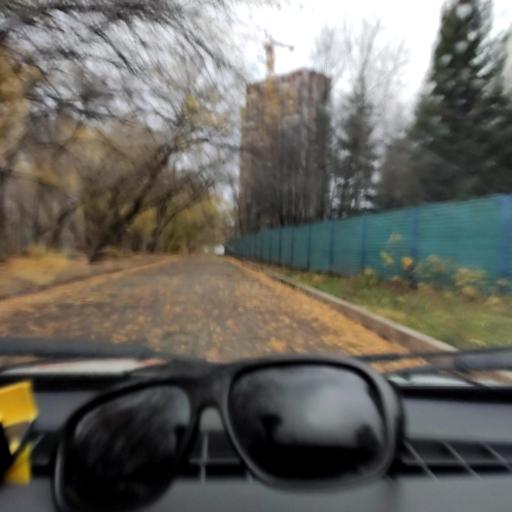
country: RU
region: Bashkortostan
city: Ufa
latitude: 54.7165
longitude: 56.0152
